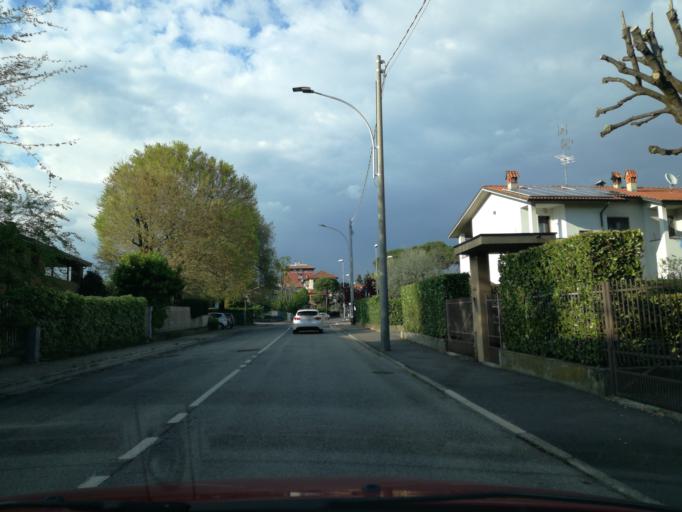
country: IT
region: Lombardy
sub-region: Provincia di Monza e Brianza
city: Carnate
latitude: 45.6457
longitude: 9.3776
